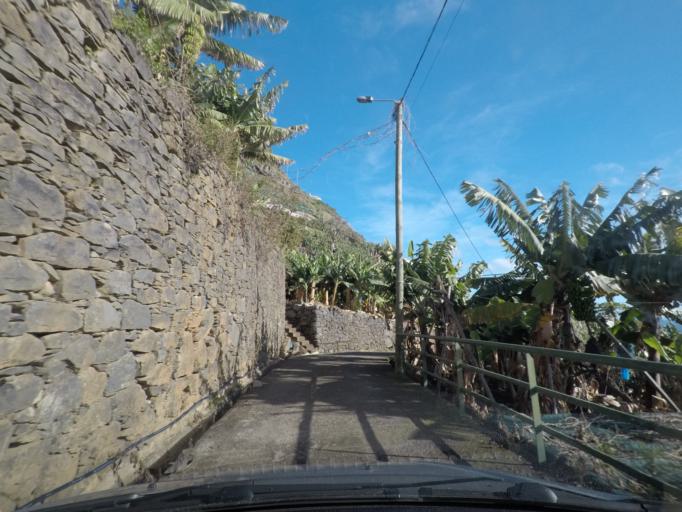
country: PT
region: Madeira
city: Ponta do Sol
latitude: 32.6896
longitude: -17.1172
